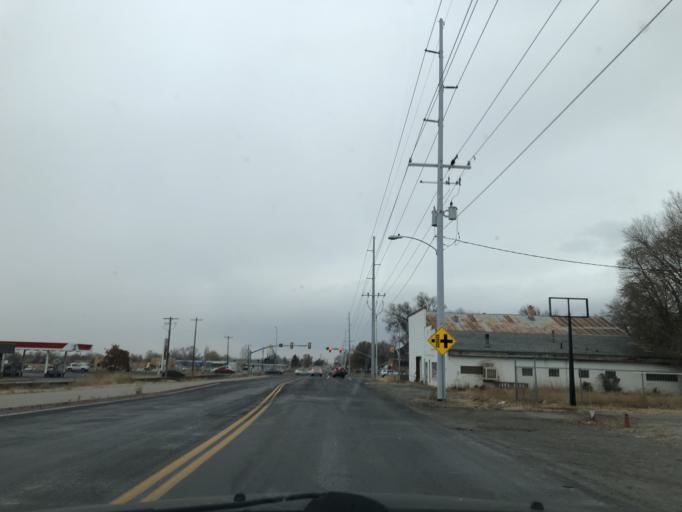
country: US
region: Utah
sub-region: Cache County
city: Logan
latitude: 41.7342
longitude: -111.8497
